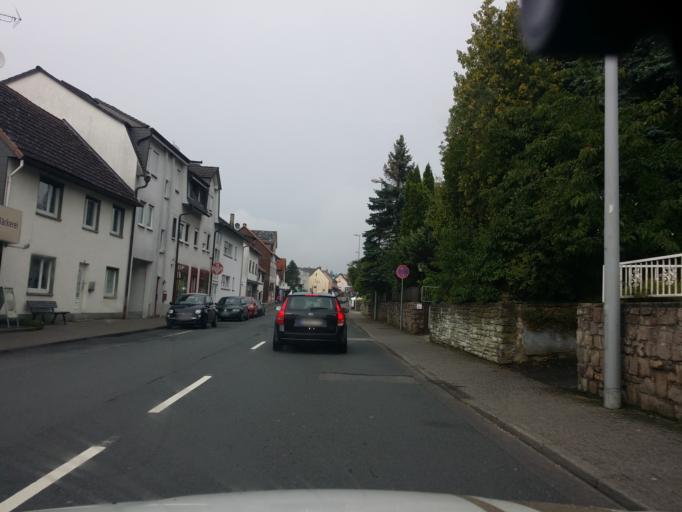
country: DE
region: Hesse
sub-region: Regierungsbezirk Darmstadt
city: Glashutten
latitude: 50.2173
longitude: 8.4031
